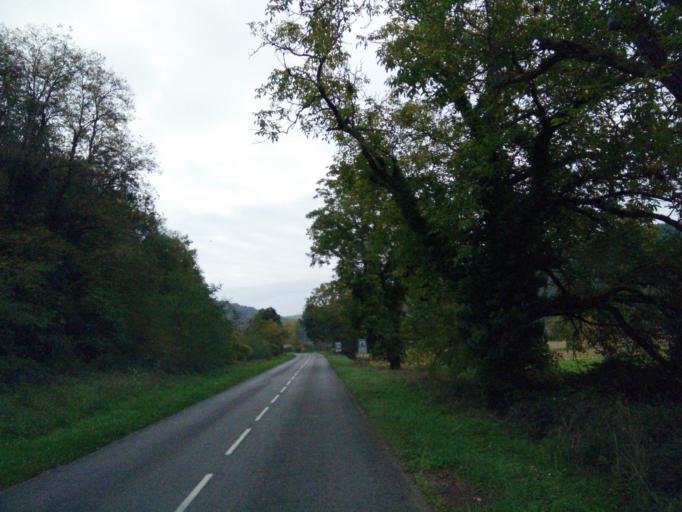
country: FR
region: Midi-Pyrenees
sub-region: Departement du Lot
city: Lalbenque
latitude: 44.4737
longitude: 1.5866
